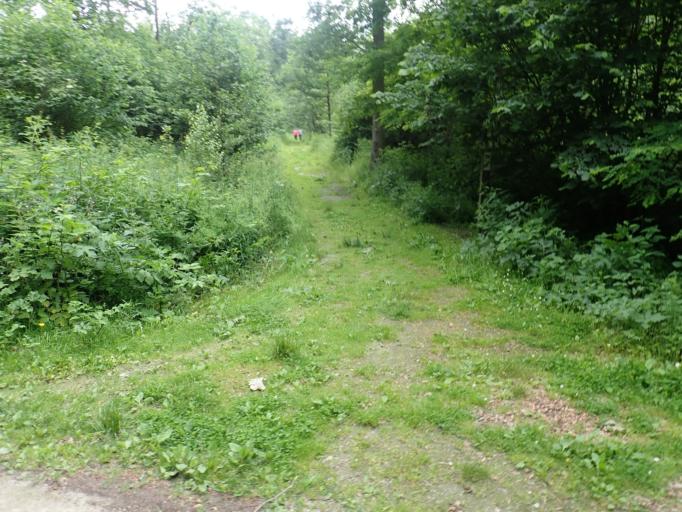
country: BE
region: Flanders
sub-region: Provincie Antwerpen
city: Heist-op-den-Berg
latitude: 51.0904
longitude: 4.7162
